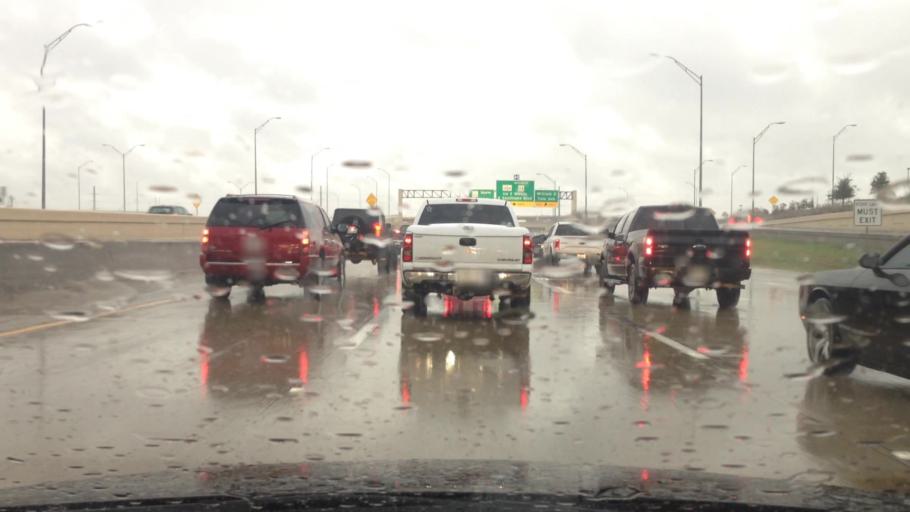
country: US
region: Texas
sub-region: Tarrant County
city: Grapevine
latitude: 32.9236
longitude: -97.0788
